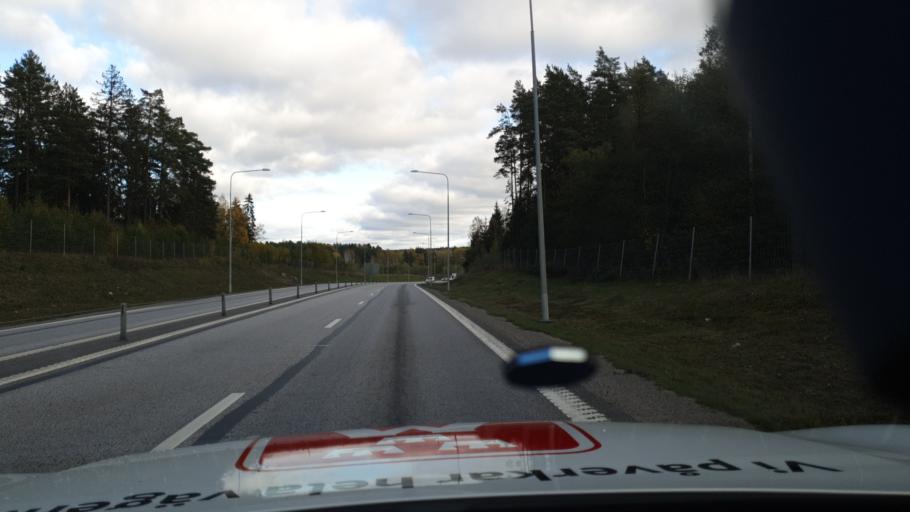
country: SE
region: Stockholm
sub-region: Taby Kommun
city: Taby
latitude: 59.4774
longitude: 18.0656
